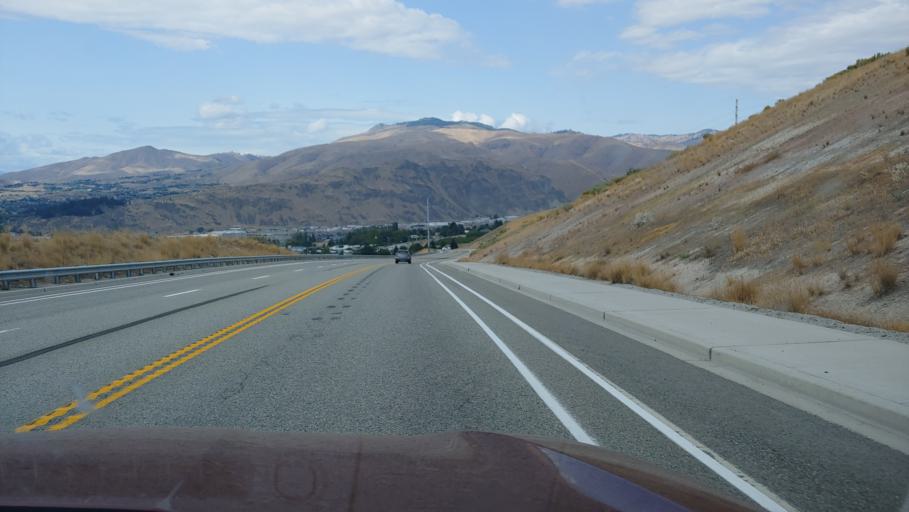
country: US
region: Washington
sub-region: Douglas County
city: East Wenatchee Bench
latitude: 47.4605
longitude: -120.2921
